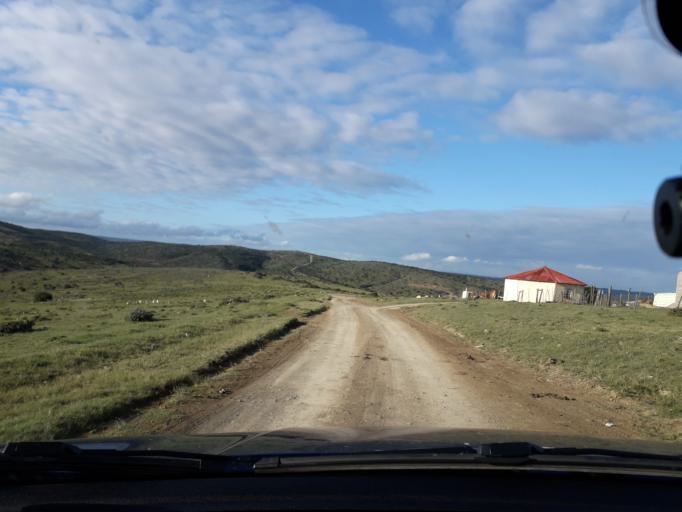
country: ZA
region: Eastern Cape
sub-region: Buffalo City Metropolitan Municipality
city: Bhisho
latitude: -33.1287
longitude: 27.4400
